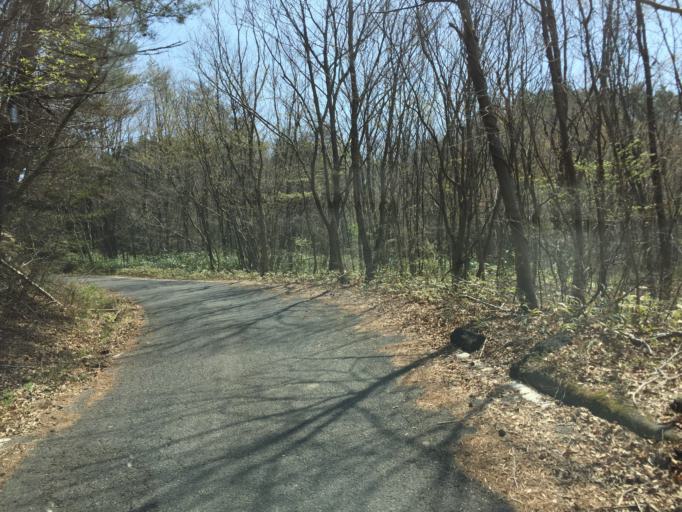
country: JP
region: Fukushima
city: Ishikawa
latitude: 36.9940
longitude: 140.5626
